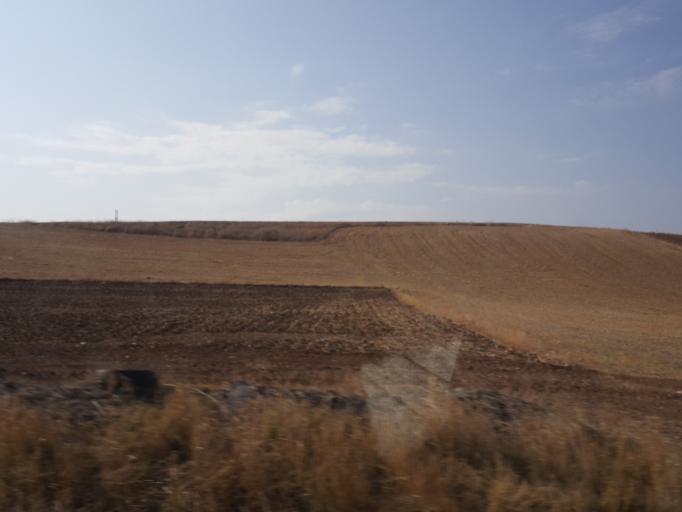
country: TR
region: Corum
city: Cemilbey
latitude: 40.1767
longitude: 35.0335
